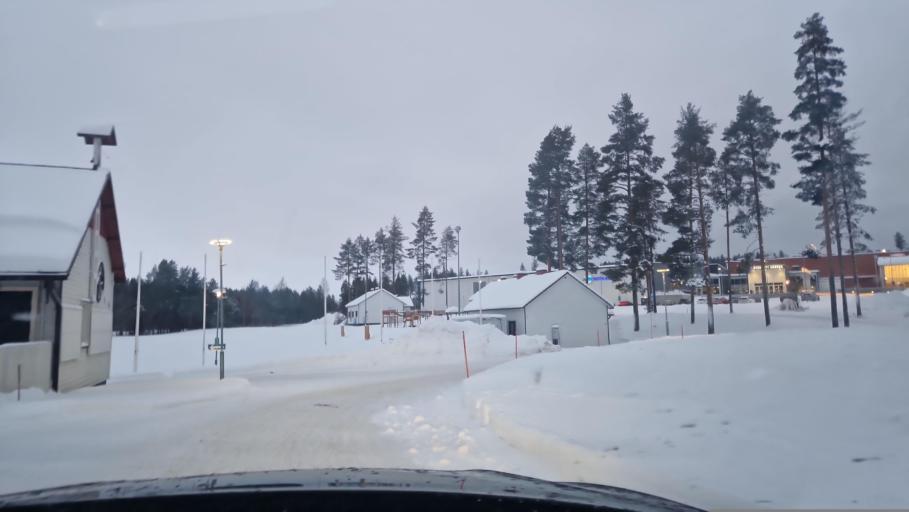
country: FI
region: Kainuu
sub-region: Kajaani
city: Vuokatti
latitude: 64.1377
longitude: 28.2858
